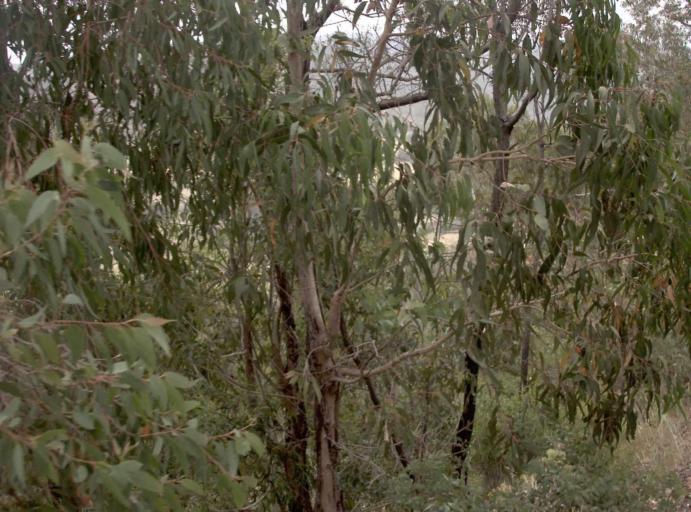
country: AU
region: Victoria
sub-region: Wellington
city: Heyfield
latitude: -37.7067
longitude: 146.6669
